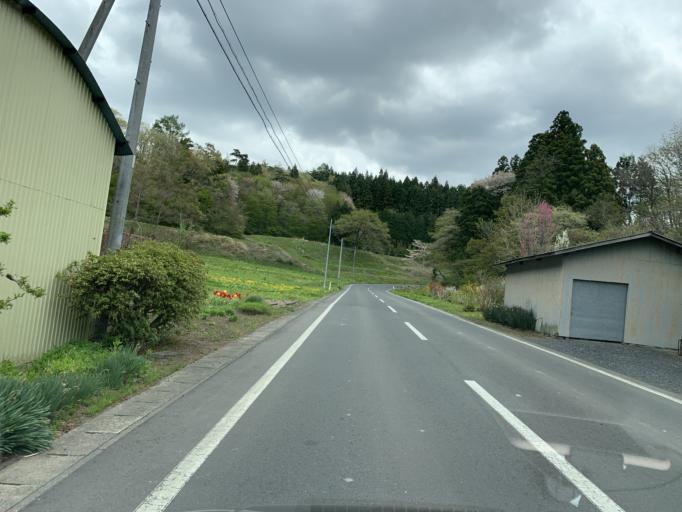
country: JP
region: Iwate
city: Ichinoseki
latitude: 38.8395
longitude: 141.3531
